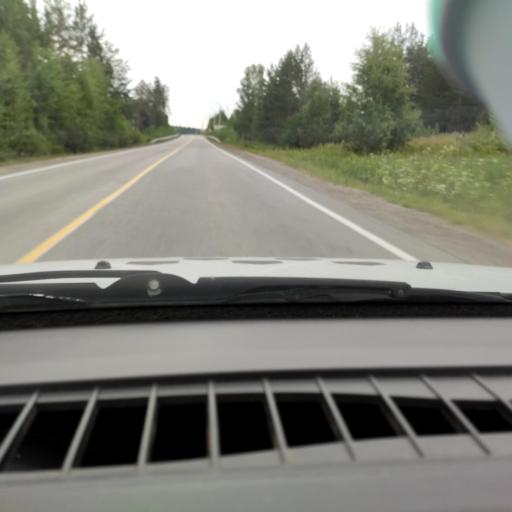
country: RU
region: Chelyabinsk
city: Kyshtym
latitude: 55.7091
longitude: 60.5080
